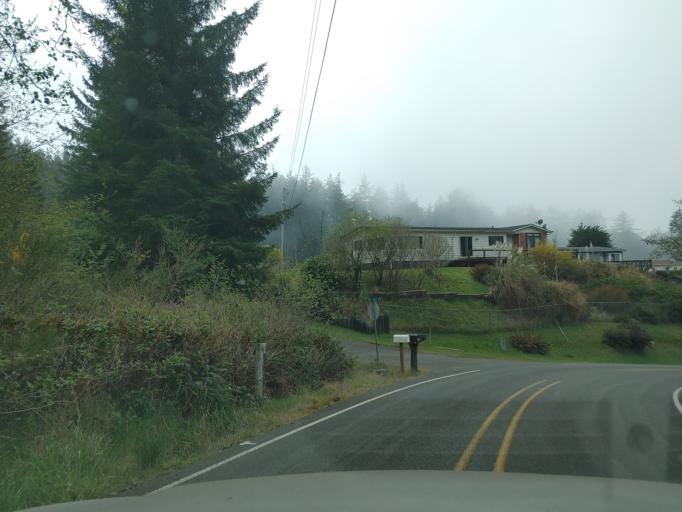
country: US
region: Oregon
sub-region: Coos County
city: Lakeside
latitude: 43.6668
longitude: -124.1940
